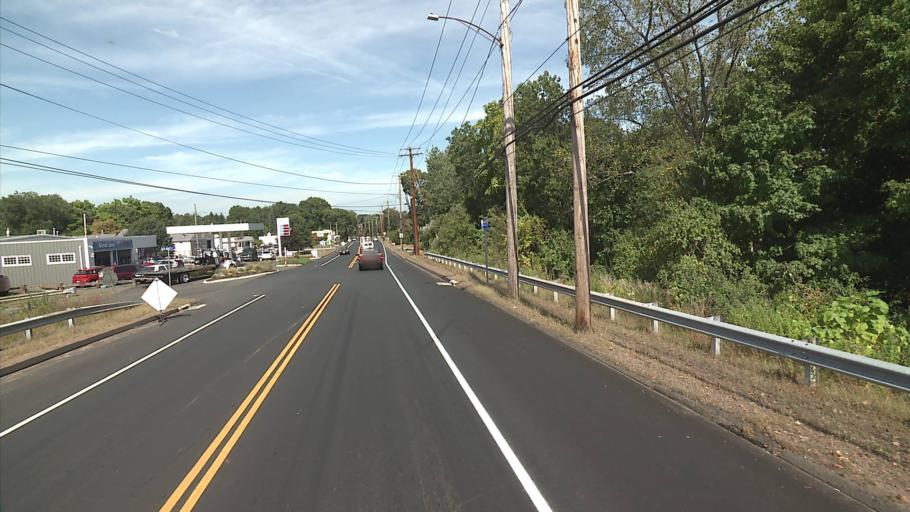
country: US
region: Connecticut
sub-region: New Haven County
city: North Haven
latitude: 41.3693
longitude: -72.8524
